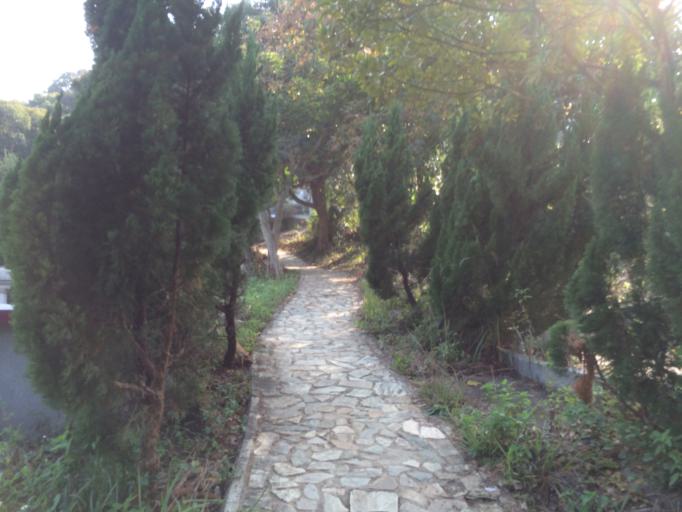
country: HK
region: Tai Po
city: Tai Po
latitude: 22.4525
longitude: 114.2142
